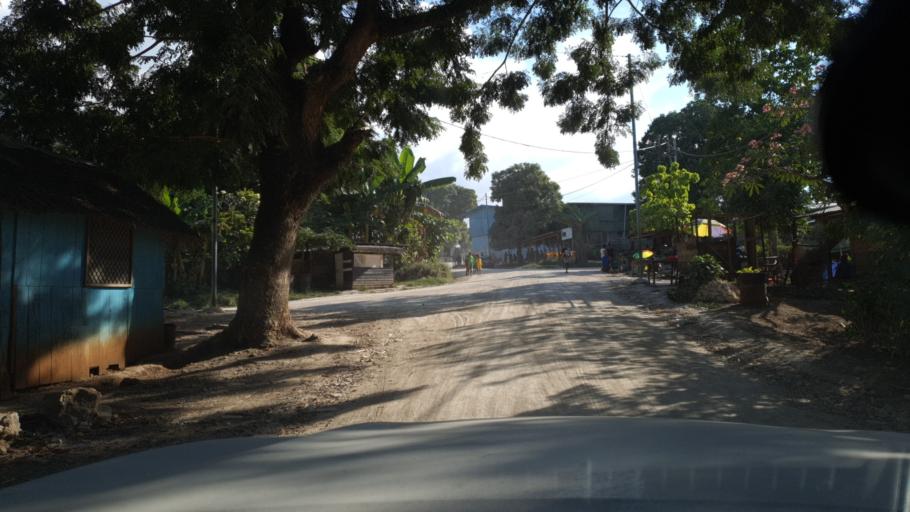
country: SB
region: Guadalcanal
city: Honiara
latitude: -9.4528
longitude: 159.9921
